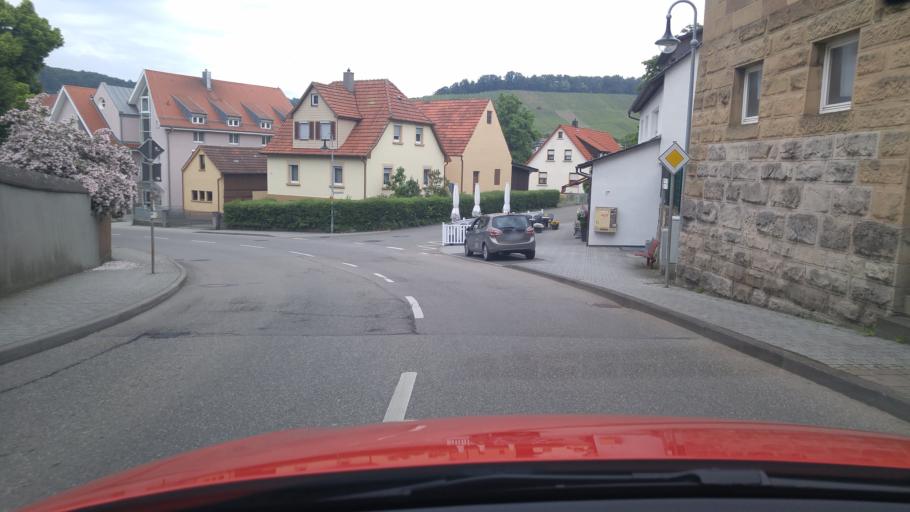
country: DE
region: Baden-Wuerttemberg
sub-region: Regierungsbezirk Stuttgart
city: Lowenstein
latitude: 49.1355
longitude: 9.3841
